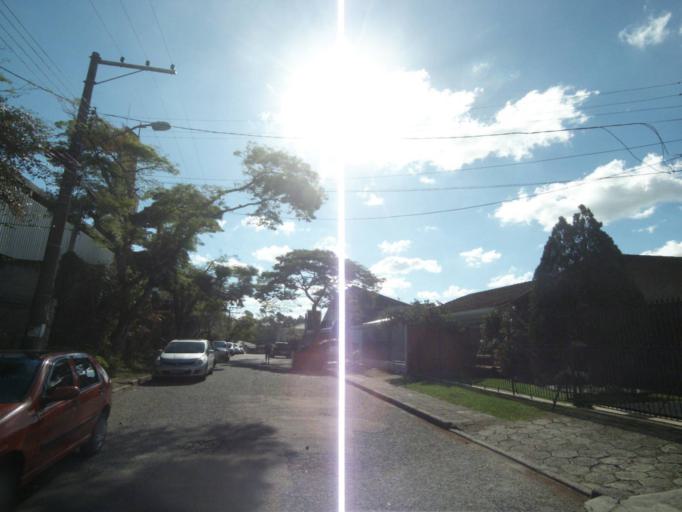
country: BR
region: Parana
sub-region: Curitiba
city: Curitiba
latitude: -25.3910
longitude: -49.2592
